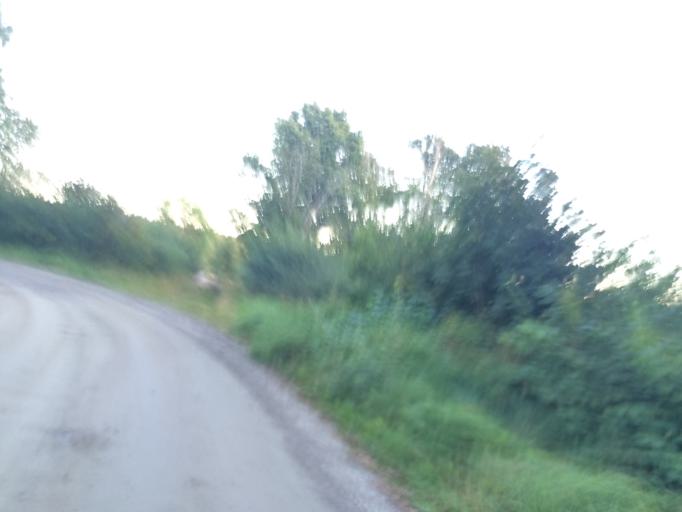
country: SE
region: Soedermanland
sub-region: Eskilstuna Kommun
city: Kvicksund
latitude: 59.4468
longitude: 16.3541
